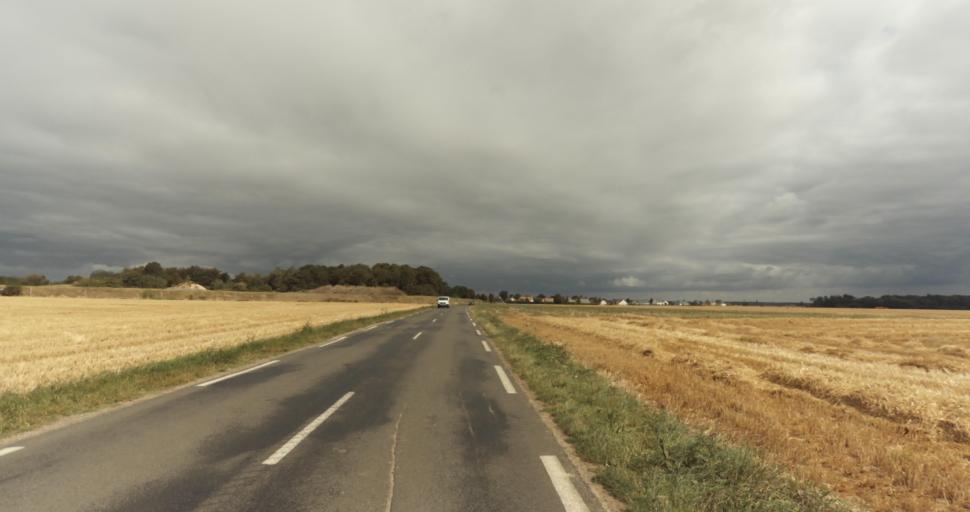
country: FR
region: Haute-Normandie
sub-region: Departement de l'Eure
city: Gravigny
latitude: 49.0259
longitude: 1.2416
